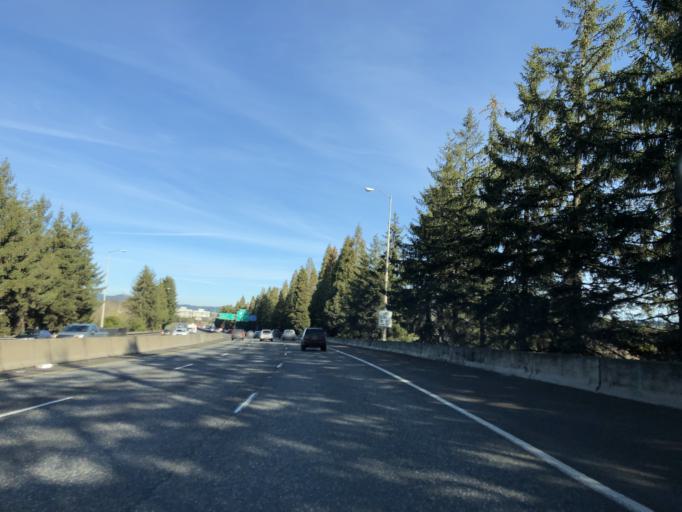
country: US
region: Oregon
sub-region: Clackamas County
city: Gladstone
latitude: 45.3671
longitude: -122.5958
